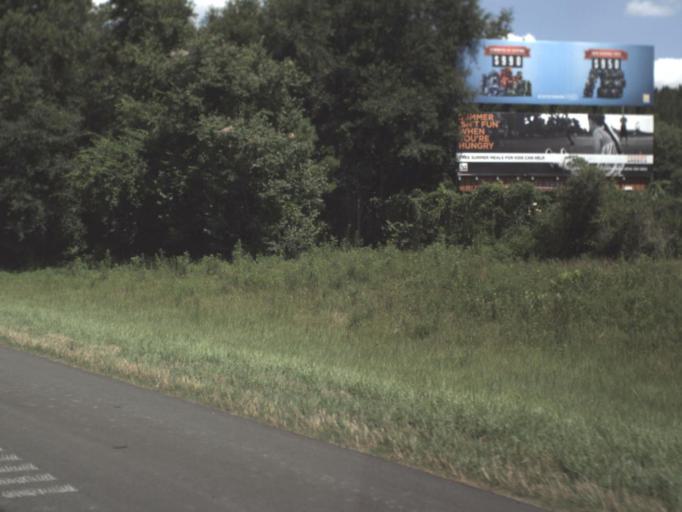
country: US
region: Florida
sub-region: Madison County
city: Madison
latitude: 30.4112
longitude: -83.4213
